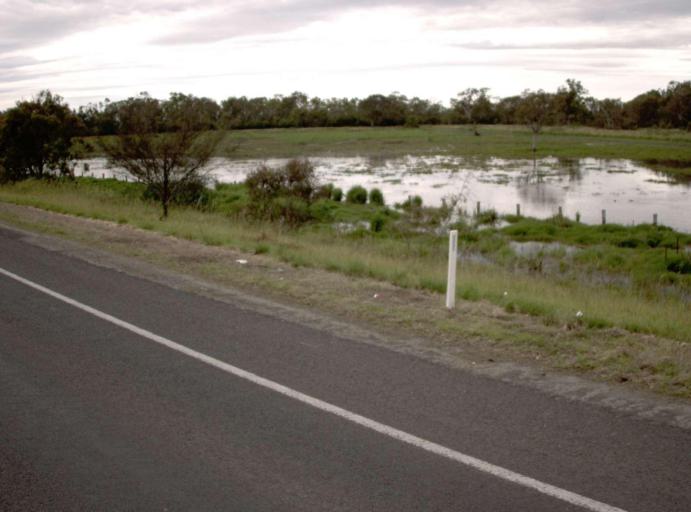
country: AU
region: Victoria
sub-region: Wellington
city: Sale
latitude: -38.1483
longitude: 147.0810
